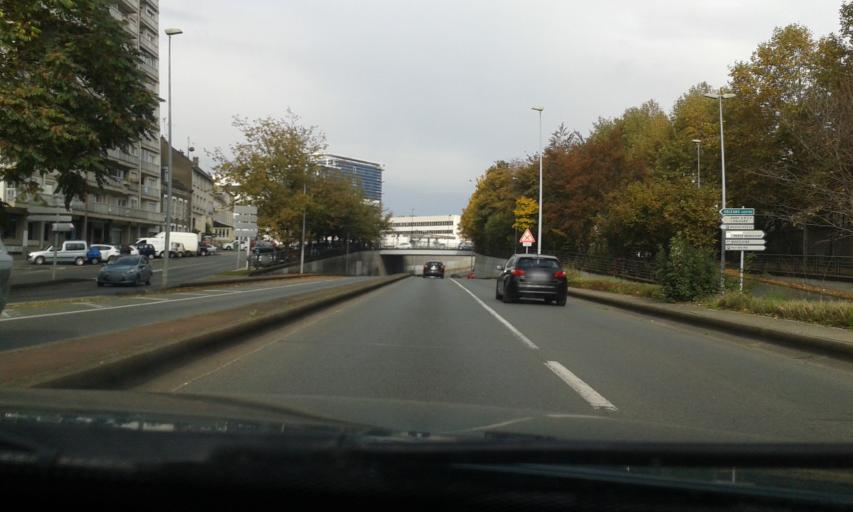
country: FR
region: Centre
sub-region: Departement du Loiret
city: Orleans
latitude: 47.9000
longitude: 1.8942
